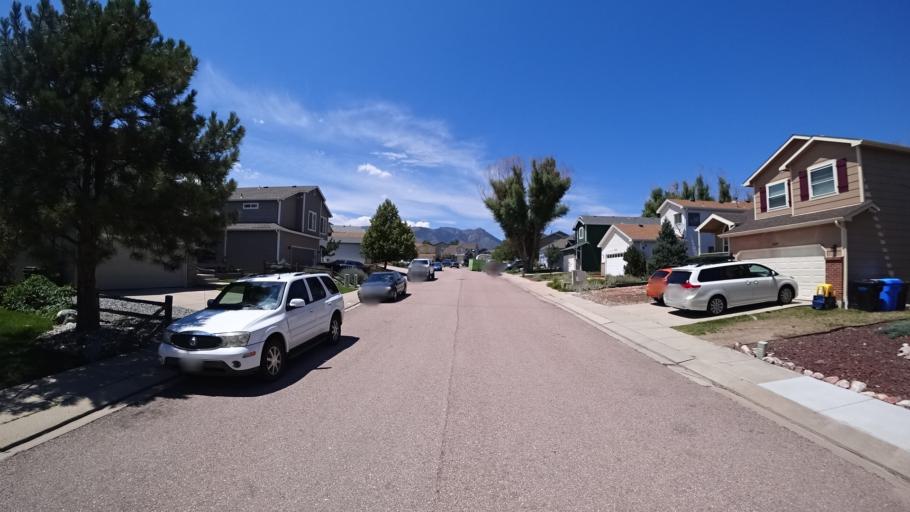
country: US
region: Colorado
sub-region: El Paso County
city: Air Force Academy
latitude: 38.9197
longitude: -104.8350
